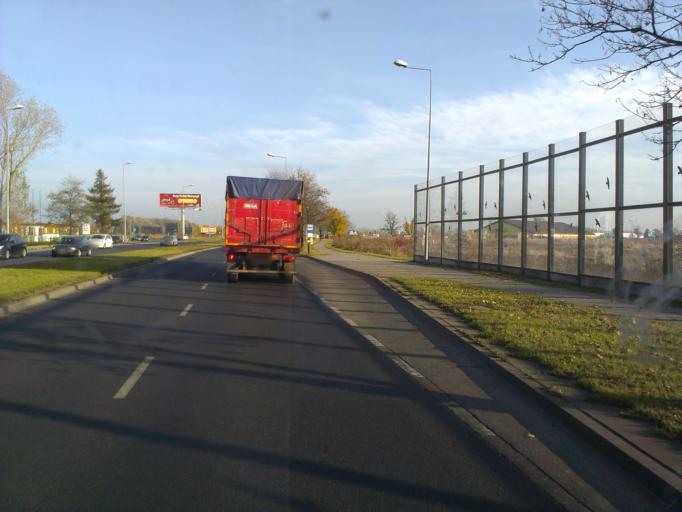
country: PL
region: Lower Silesian Voivodeship
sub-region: Legnica
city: Legnica
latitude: 51.1761
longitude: 16.1675
